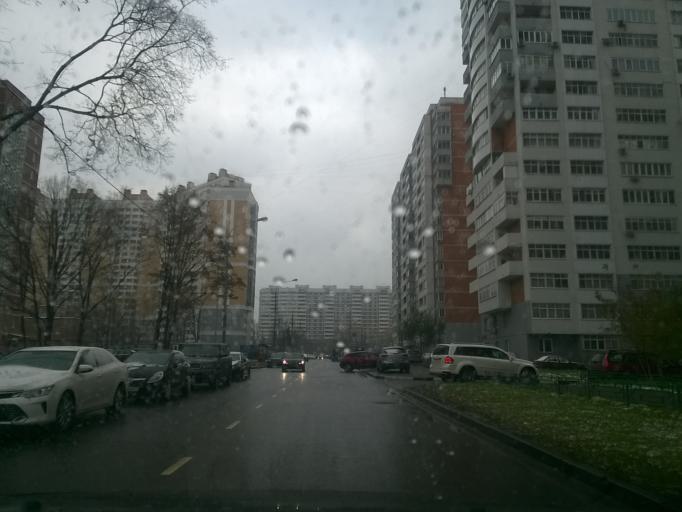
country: RU
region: Moskovskaya
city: Bol'shaya Setun'
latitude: 55.7362
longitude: 37.4314
